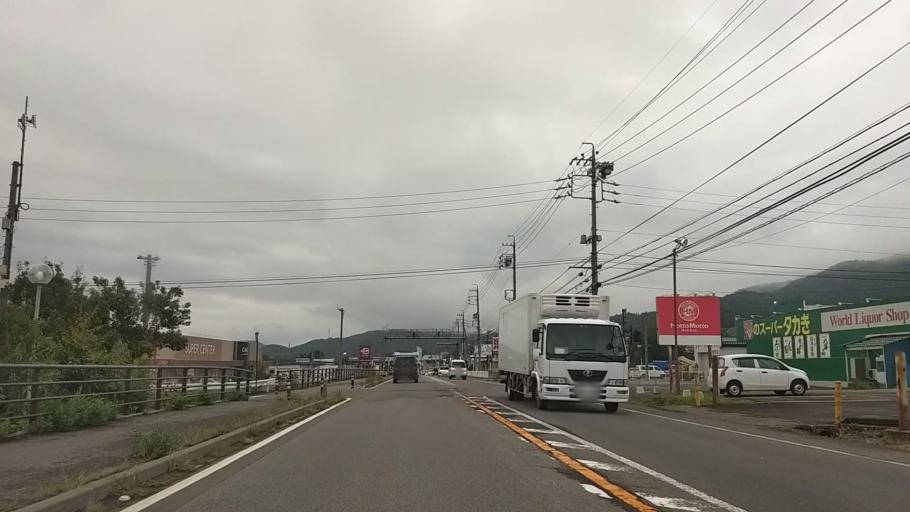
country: JP
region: Nagano
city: Iiyama
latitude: 36.8334
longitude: 138.3566
